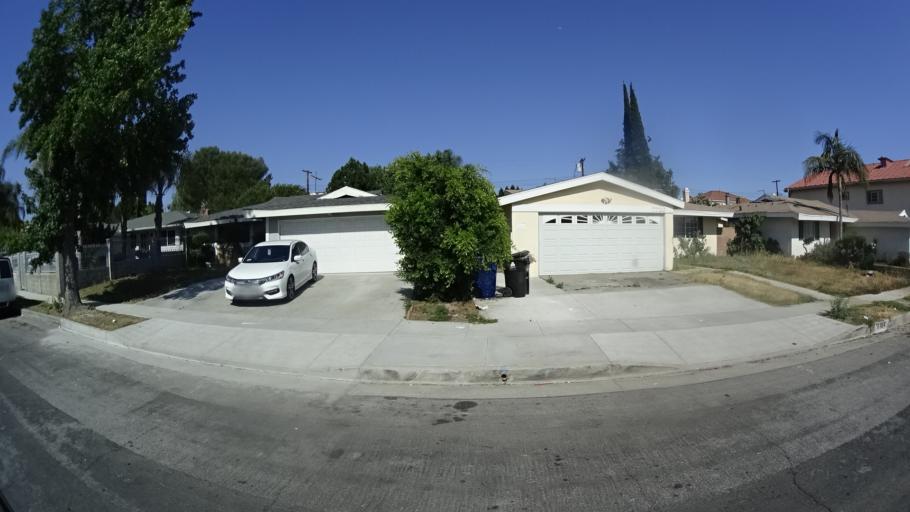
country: US
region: California
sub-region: Los Angeles County
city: Van Nuys
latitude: 34.2110
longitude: -118.4158
